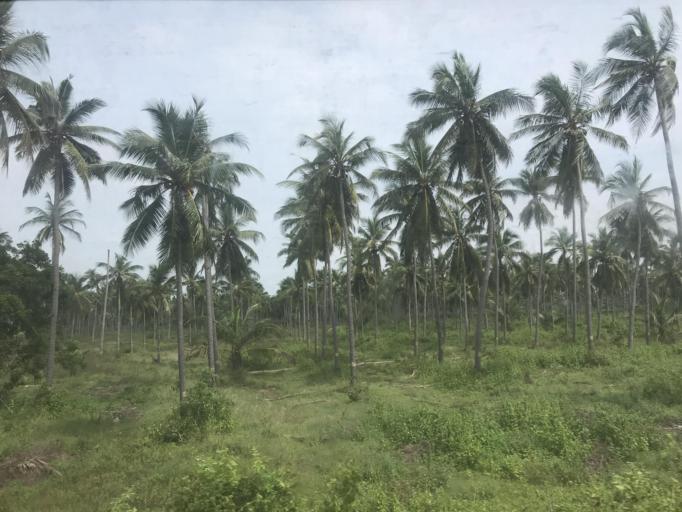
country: LK
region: Northern Province
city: Kilinochchi
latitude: 9.5817
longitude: 80.3529
